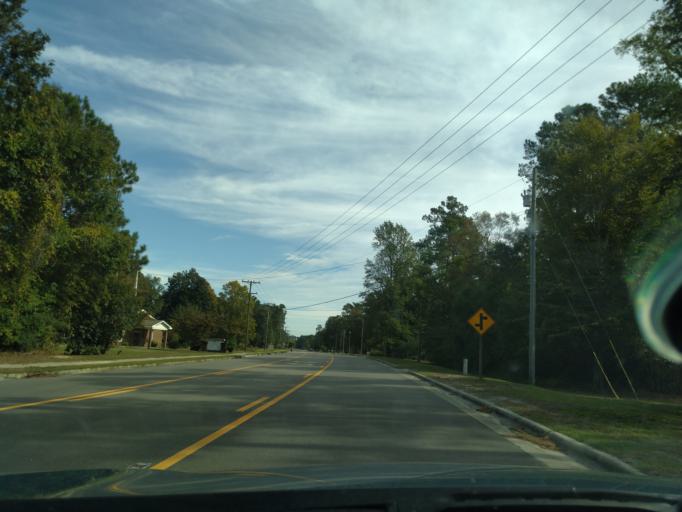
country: US
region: North Carolina
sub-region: Beaufort County
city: River Road
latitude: 35.5079
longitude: -76.9973
